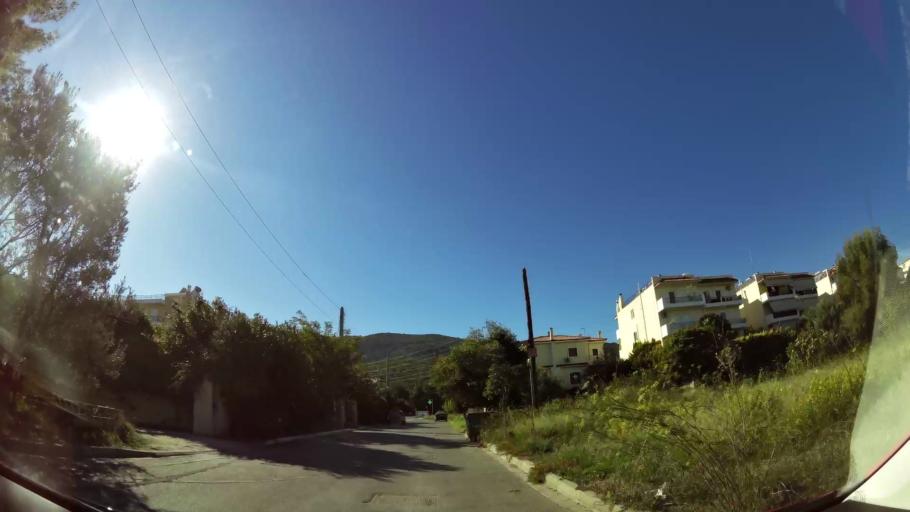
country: GR
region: Attica
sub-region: Nomarchia Anatolikis Attikis
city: Leondarion
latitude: 37.9898
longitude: 23.8482
